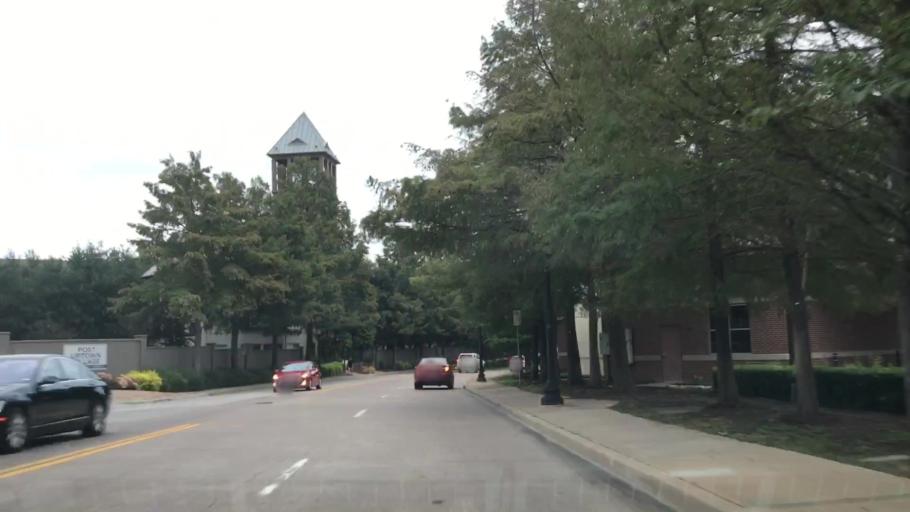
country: US
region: Texas
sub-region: Dallas County
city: Dallas
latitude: 32.7932
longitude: -96.7995
